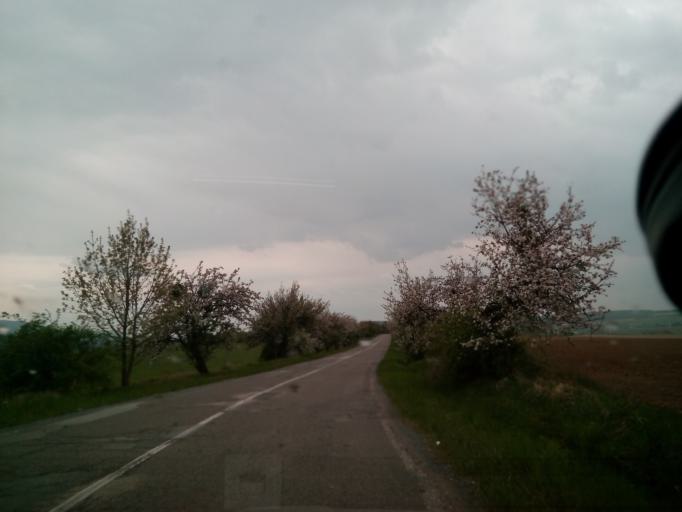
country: SK
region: Kosicky
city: Secovce
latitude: 48.7528
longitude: 21.4645
